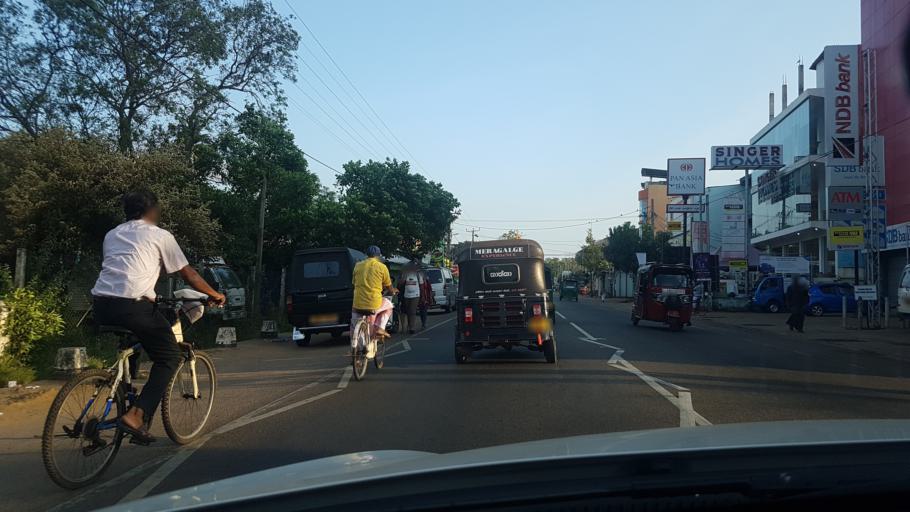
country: LK
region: North Western
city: Chilaw
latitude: 7.5739
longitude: 79.7969
